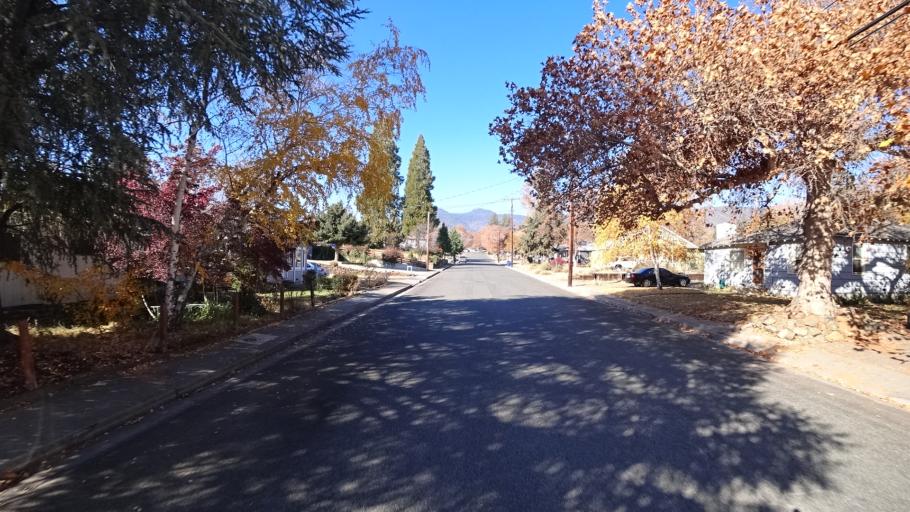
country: US
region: California
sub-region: Siskiyou County
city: Yreka
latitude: 41.7353
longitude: -122.6438
